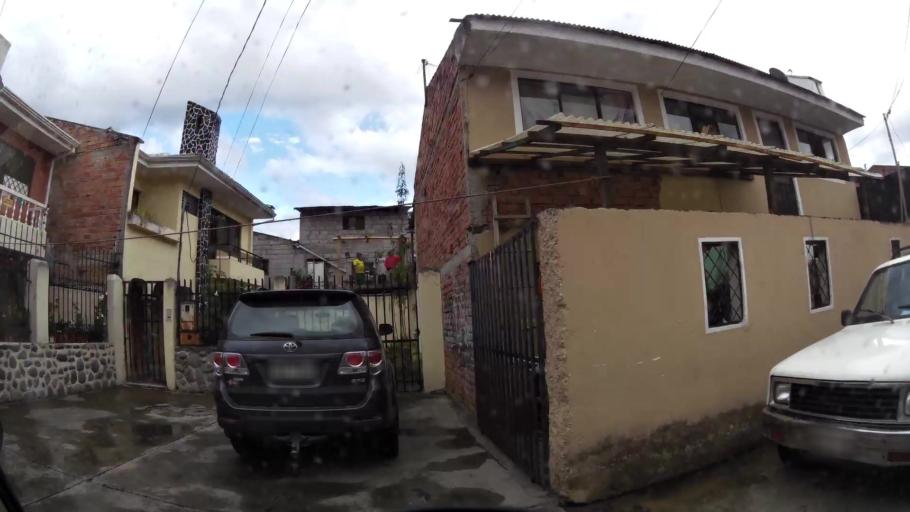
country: EC
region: Azuay
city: Cuenca
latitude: -2.9006
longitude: -79.0235
